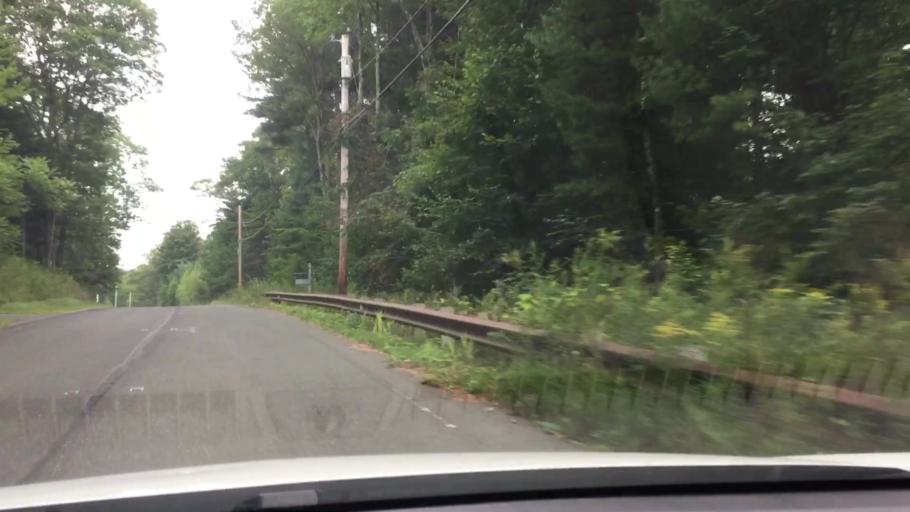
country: US
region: Massachusetts
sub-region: Berkshire County
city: Becket
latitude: 42.2608
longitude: -73.0004
